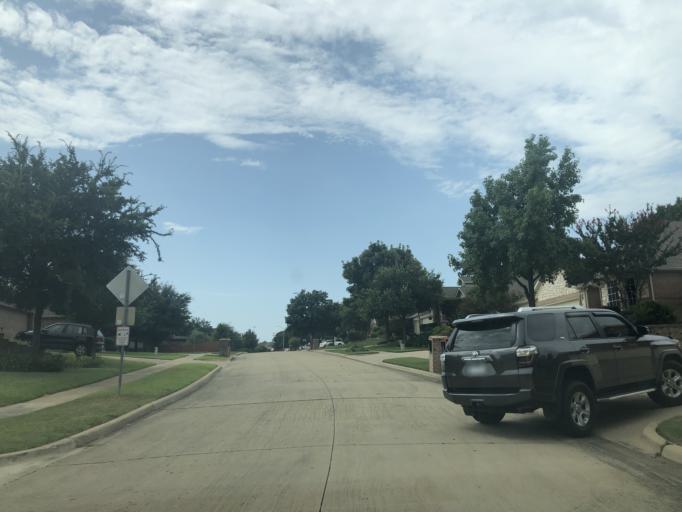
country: US
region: Texas
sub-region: Dallas County
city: Grand Prairie
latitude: 32.7669
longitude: -97.0415
